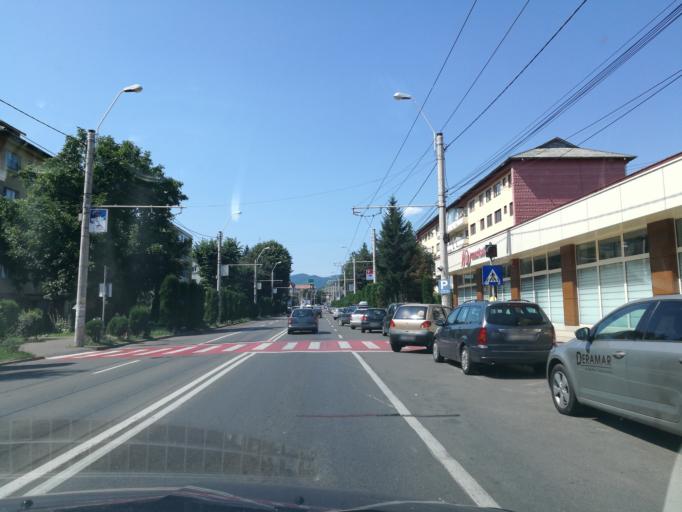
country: RO
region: Neamt
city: Piatra Neamt
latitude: 46.9349
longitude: 26.3558
